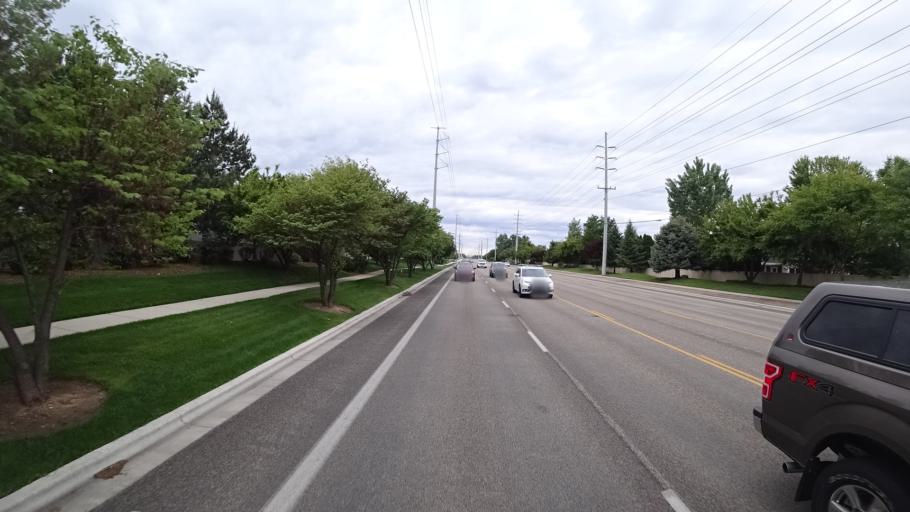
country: US
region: Idaho
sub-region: Ada County
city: Meridian
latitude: 43.6483
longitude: -116.3661
